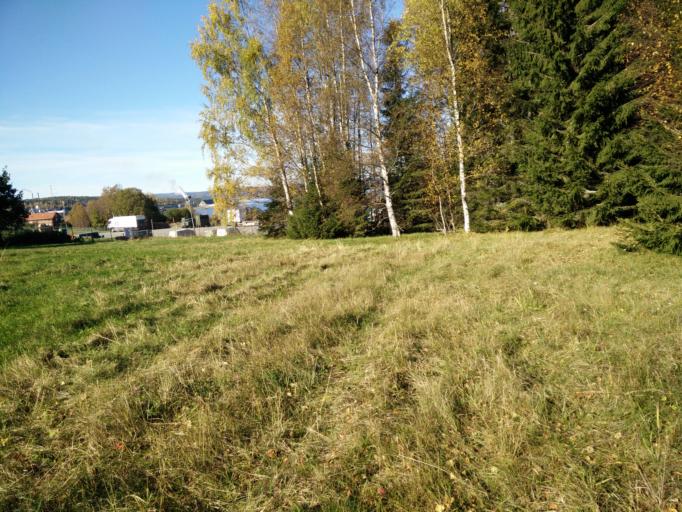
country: SE
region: Vaesternorrland
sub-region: Haernoesands Kommun
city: Haernoesand
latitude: 62.6401
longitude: 17.9702
